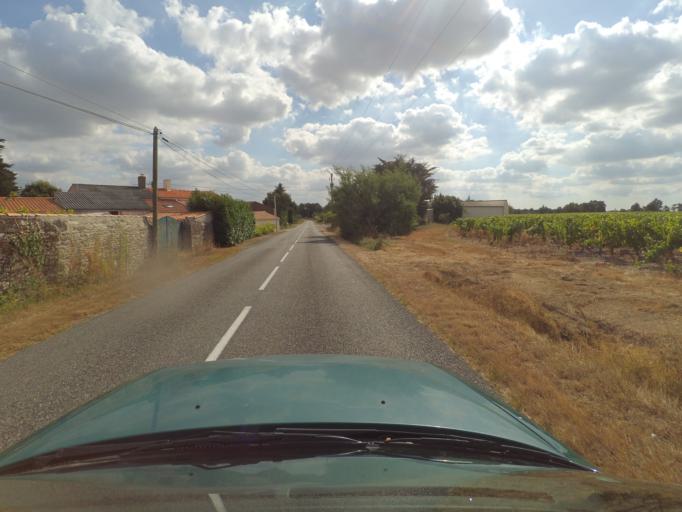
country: FR
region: Pays de la Loire
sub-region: Departement de la Loire-Atlantique
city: Aigrefeuille-sur-Maine
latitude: 47.0582
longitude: -1.4125
